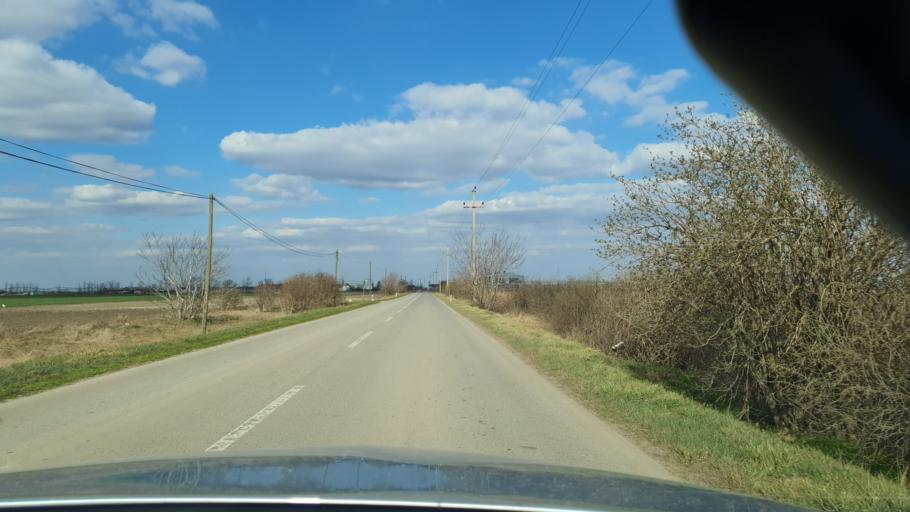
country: RS
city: Kulpin
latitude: 45.4155
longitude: 19.5954
